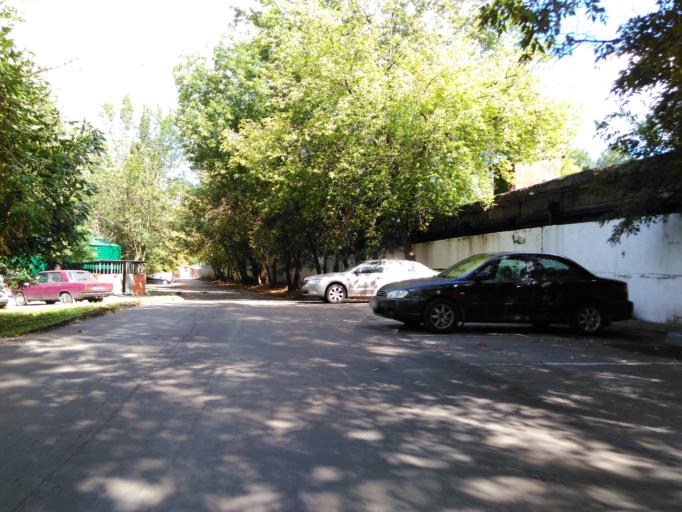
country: RU
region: Moscow
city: Novyye Cheremushki
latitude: 55.6944
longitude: 37.6138
